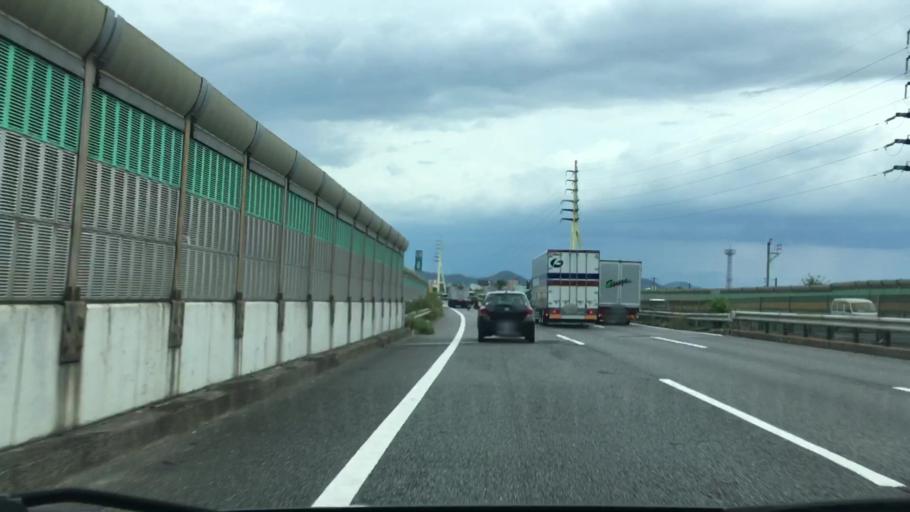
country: JP
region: Hyogo
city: Himeji
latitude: 34.8051
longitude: 134.7028
